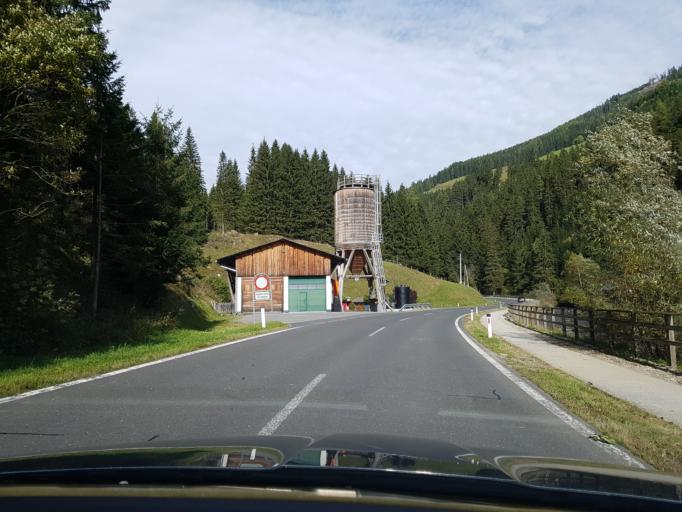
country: AT
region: Carinthia
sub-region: Politischer Bezirk Spittal an der Drau
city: Kleinkirchheim
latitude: 46.8605
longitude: 13.8906
